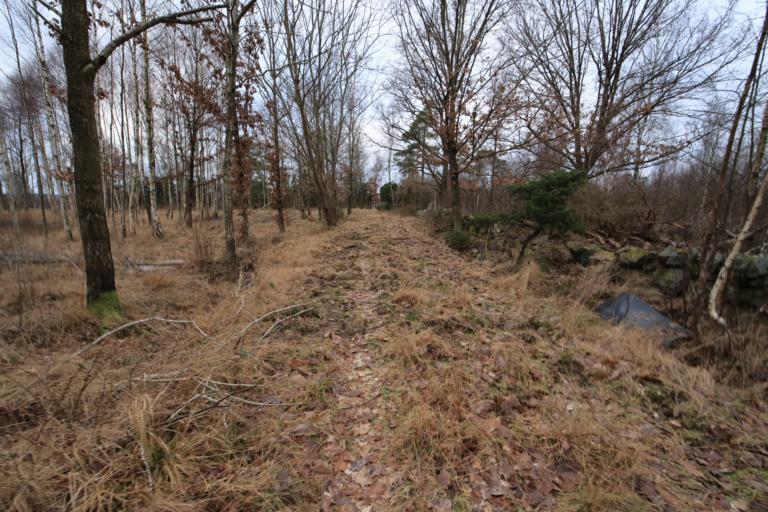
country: SE
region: Halland
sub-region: Varbergs Kommun
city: Varberg
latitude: 57.1524
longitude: 12.2894
